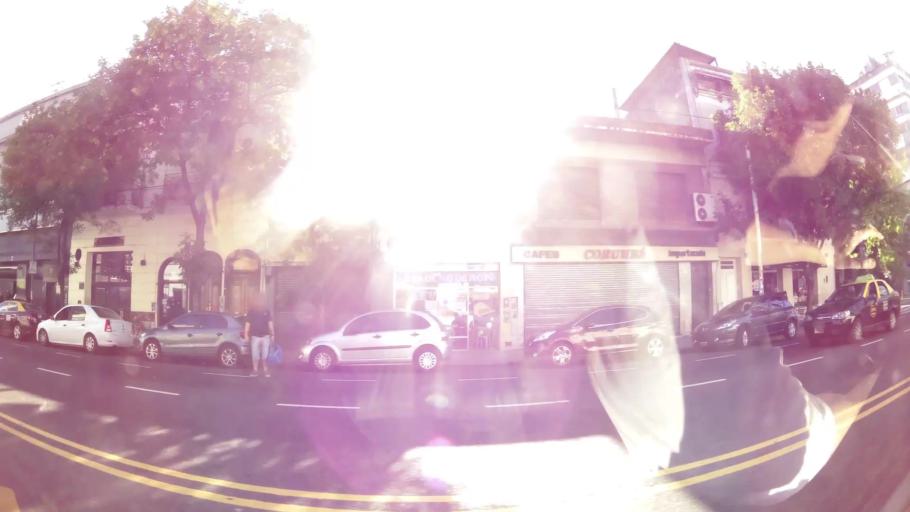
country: AR
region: Buenos Aires F.D.
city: Buenos Aires
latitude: -34.6238
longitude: -58.4274
